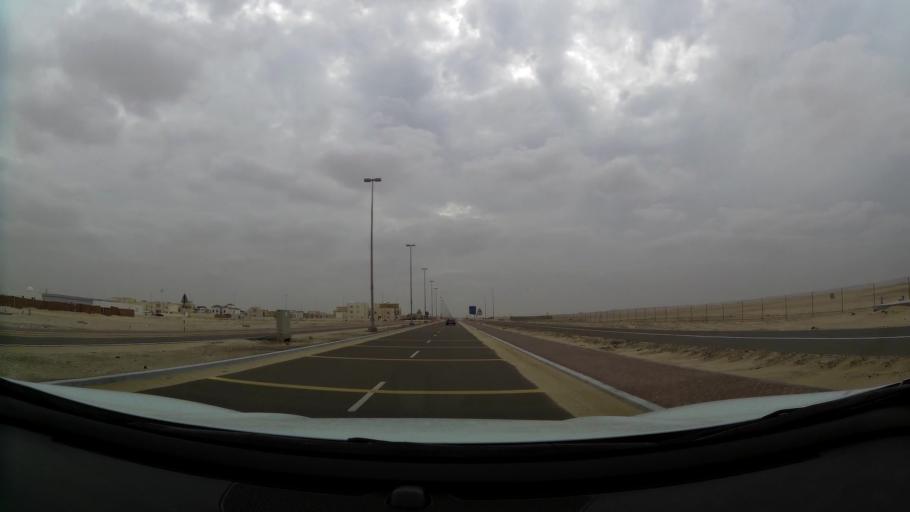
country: AE
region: Abu Dhabi
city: Abu Dhabi
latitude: 24.3708
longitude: 54.6248
